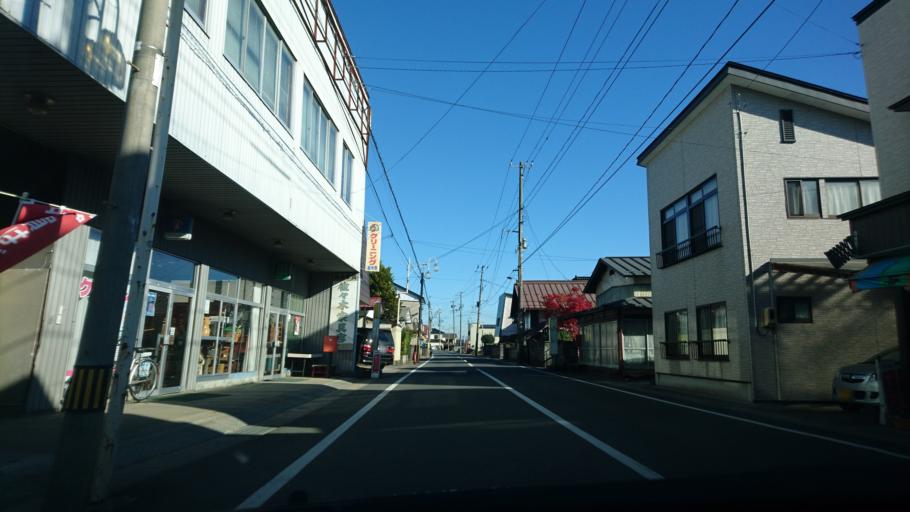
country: JP
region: Iwate
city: Mizusawa
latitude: 39.0429
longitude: 141.1204
